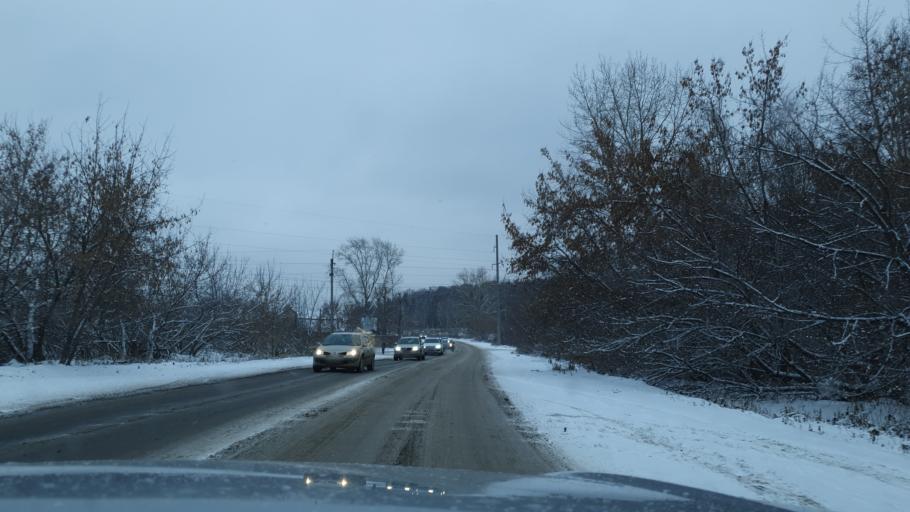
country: RU
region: Sverdlovsk
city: Istok
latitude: 56.7803
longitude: 60.7418
